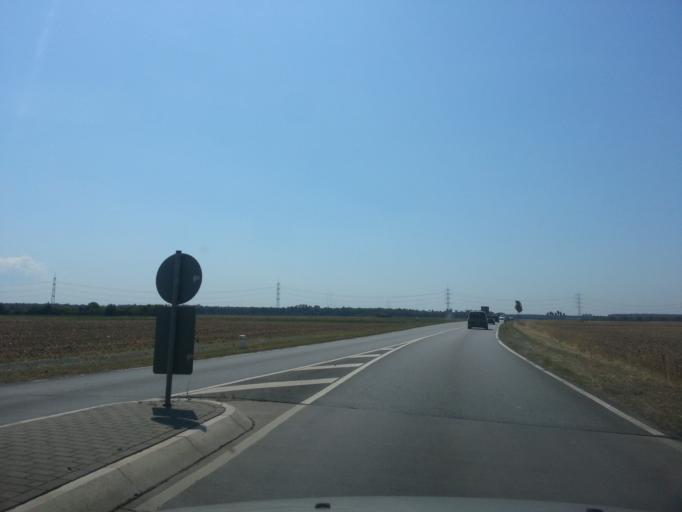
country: DE
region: Hesse
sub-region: Regierungsbezirk Darmstadt
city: Gross-Rohrheim
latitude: 49.7154
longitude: 8.4918
